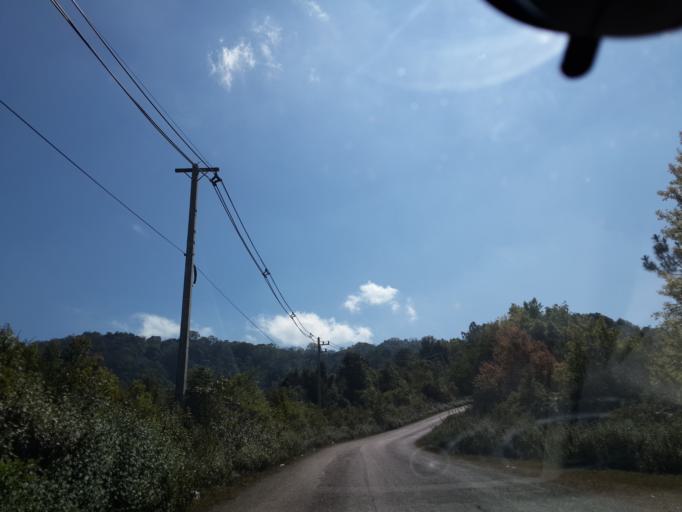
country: TH
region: Chiang Mai
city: Fang
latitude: 19.9057
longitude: 99.0535
